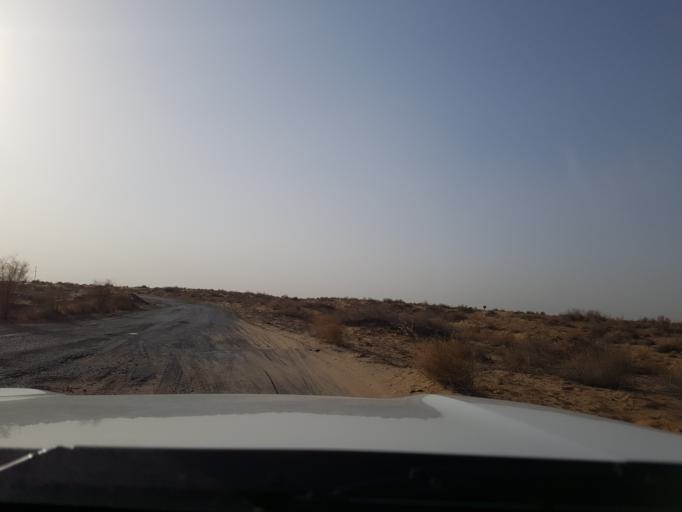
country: UZ
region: Xorazm
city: Hazorasp
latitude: 41.1917
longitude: 60.8952
